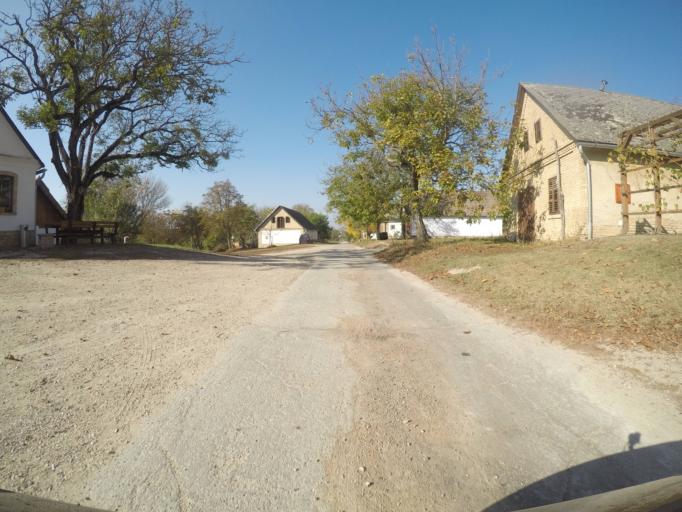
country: HU
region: Tolna
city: Nagydorog
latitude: 46.6351
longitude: 18.7045
